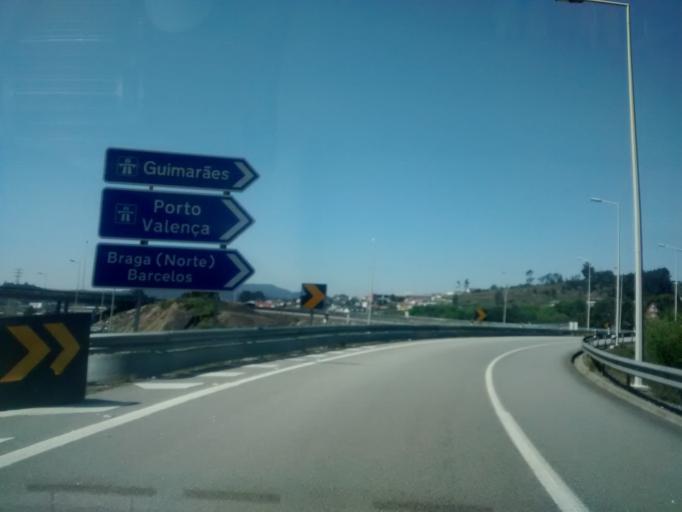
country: PT
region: Braga
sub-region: Braga
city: Braga
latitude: 41.5197
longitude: -8.4410
